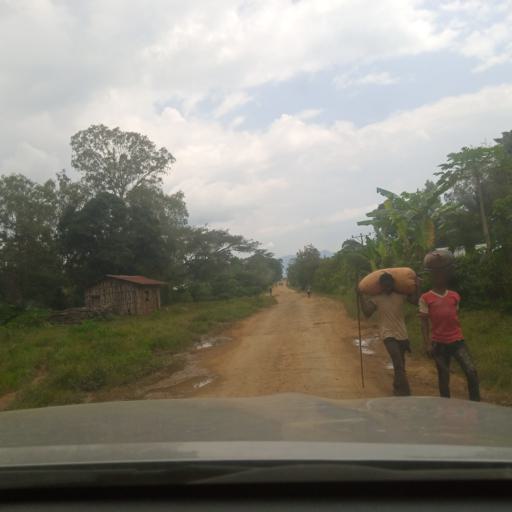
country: ET
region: Southern Nations, Nationalities, and People's Region
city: Tippi
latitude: 7.1374
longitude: 35.4222
